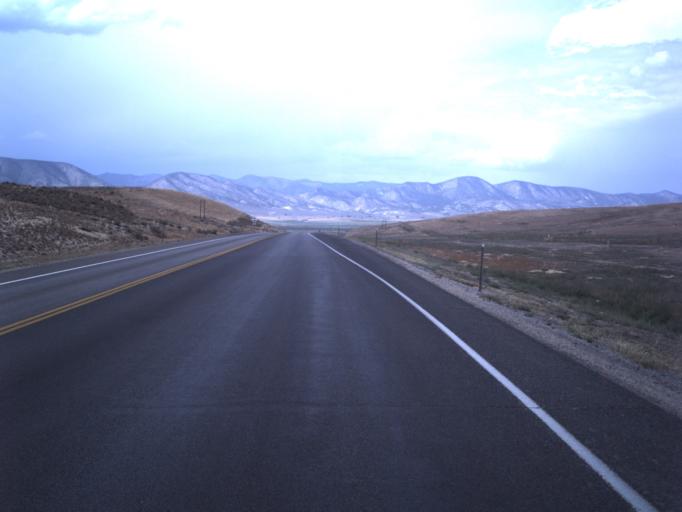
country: US
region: Utah
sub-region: Sanpete County
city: Gunnison
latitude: 39.1689
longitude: -111.8233
